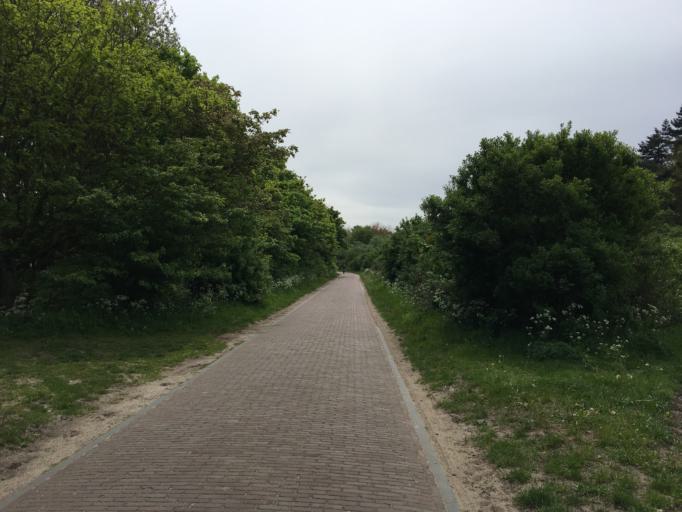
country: NL
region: North Holland
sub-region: Gemeente Bergen
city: Egmond aan Zee
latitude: 52.6149
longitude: 4.6389
